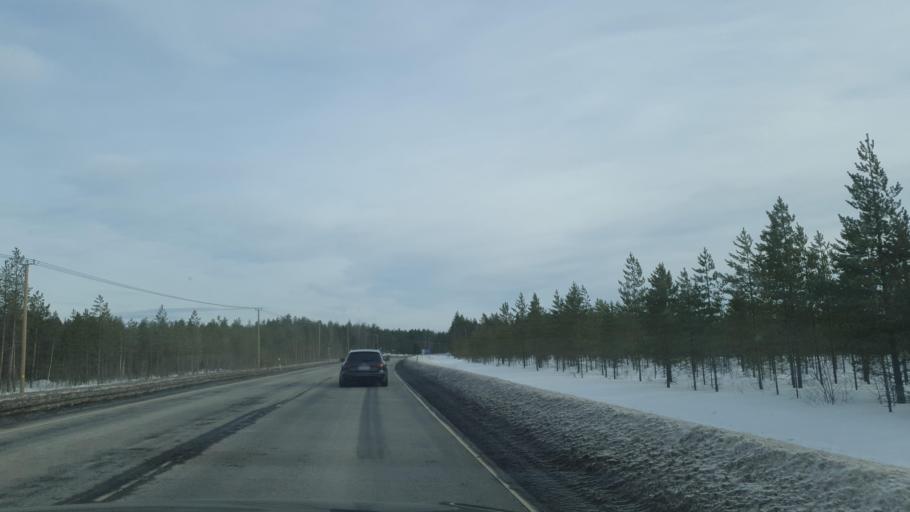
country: FI
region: Northern Ostrobothnia
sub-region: Oulu
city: Muhos
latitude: 64.7866
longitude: 26.2399
